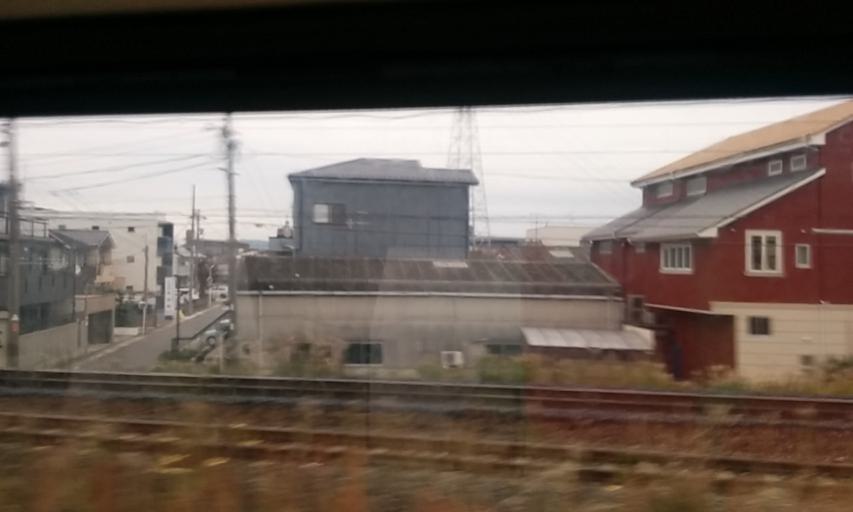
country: JP
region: Aichi
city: Kasugai
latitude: 35.2088
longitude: 136.9520
